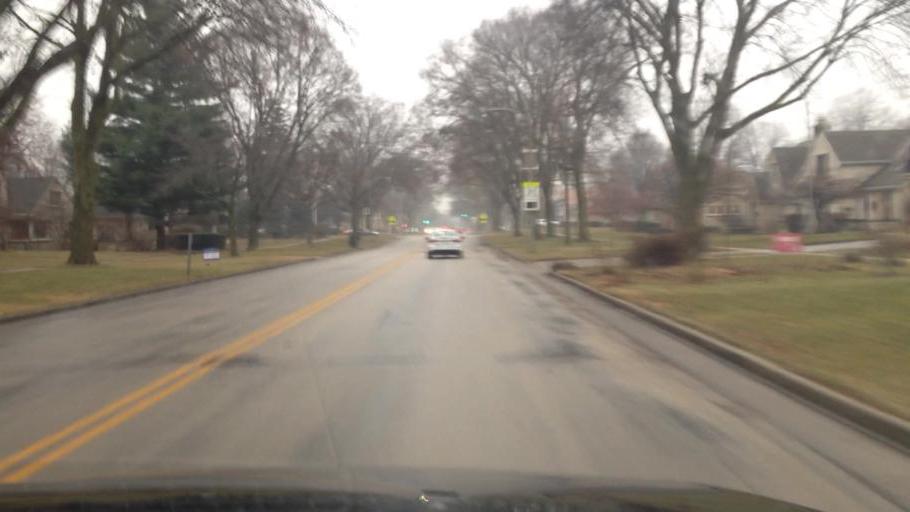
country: US
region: Wisconsin
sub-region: Milwaukee County
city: Wauwatosa
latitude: 43.0636
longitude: -88.0276
